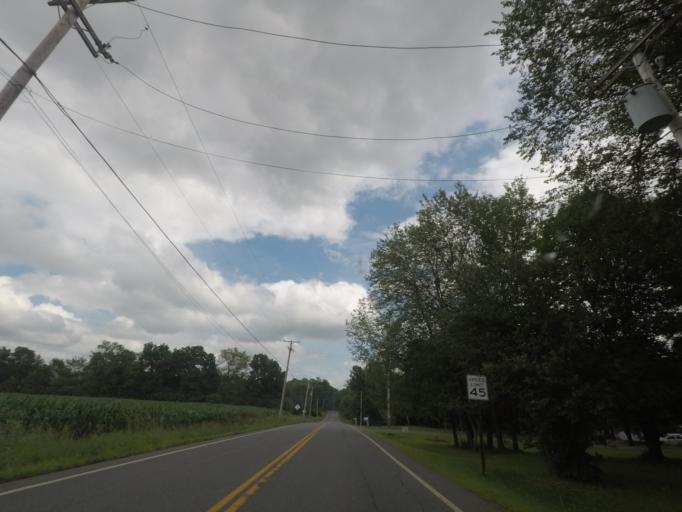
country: US
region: New York
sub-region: Saratoga County
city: Stillwater
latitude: 43.0041
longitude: -73.7045
